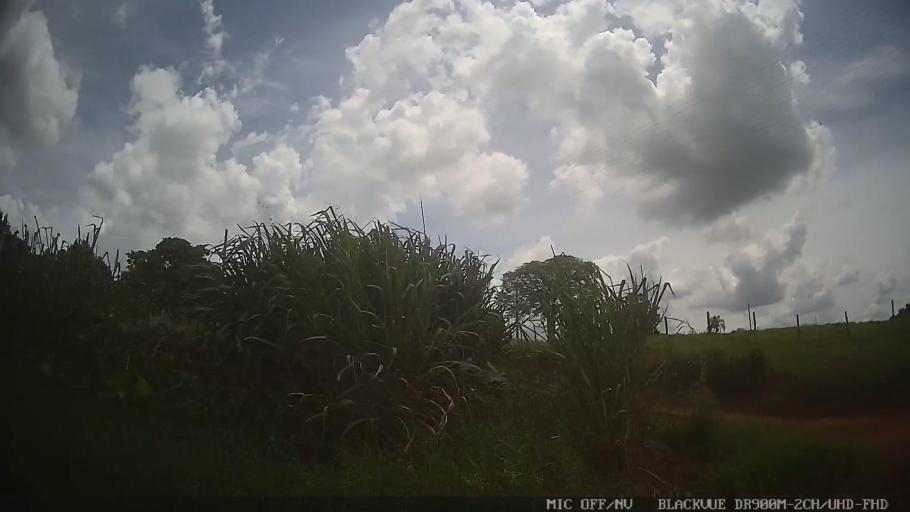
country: BR
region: Sao Paulo
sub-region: Atibaia
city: Atibaia
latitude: -23.0548
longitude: -46.5091
